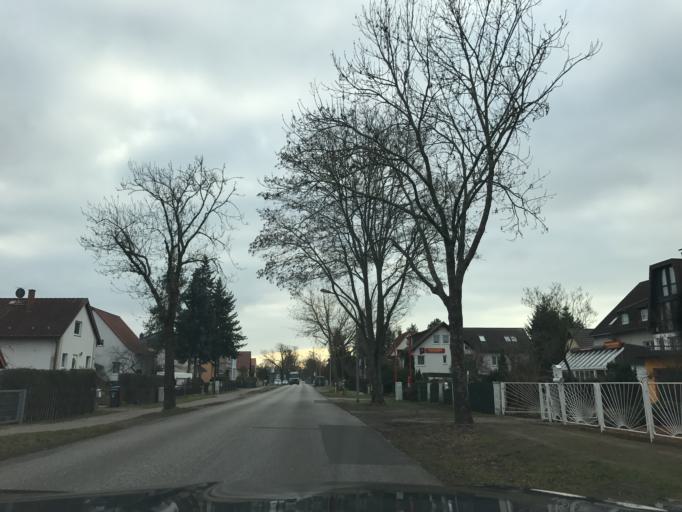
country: DE
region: Brandenburg
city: Brandenburg an der Havel
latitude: 52.3900
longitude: 12.5454
